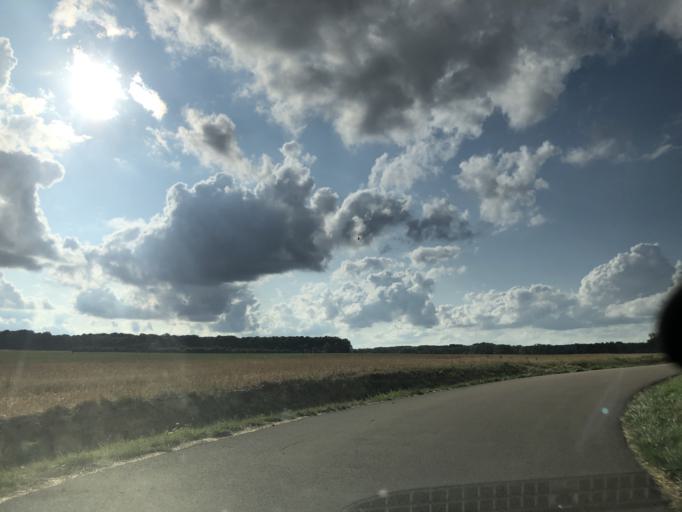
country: FR
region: Bourgogne
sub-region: Departement de l'Yonne
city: Charbuy
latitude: 47.8207
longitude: 3.4970
